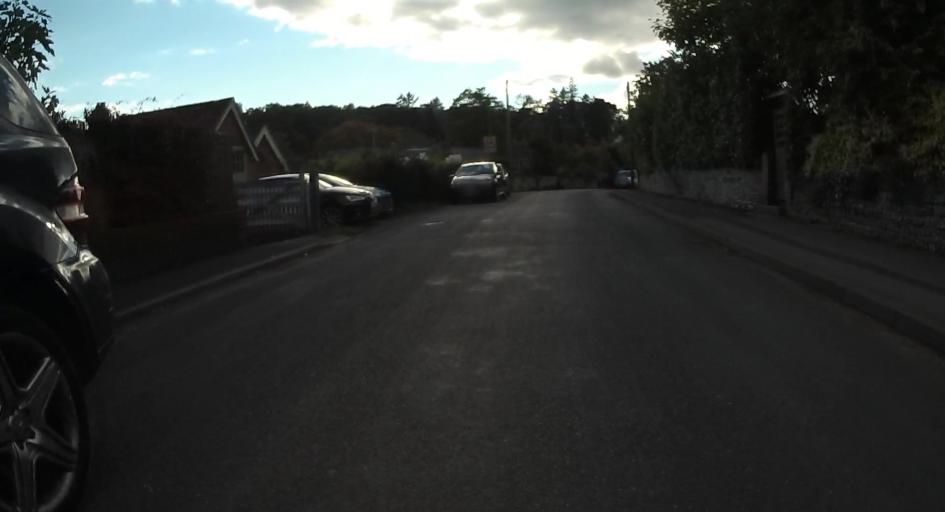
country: GB
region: England
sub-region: Surrey
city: Farnham
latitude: 51.1969
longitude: -0.7877
